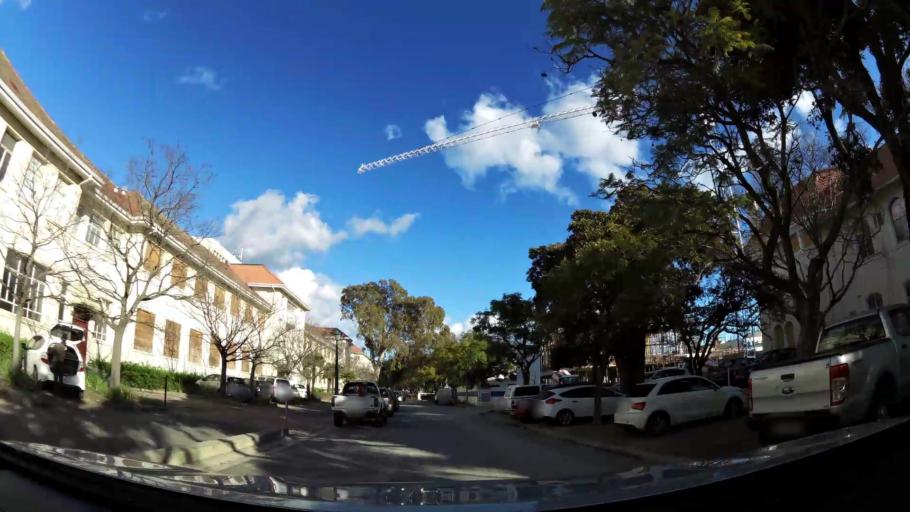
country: ZA
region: Western Cape
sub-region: Cape Winelands District Municipality
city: Stellenbosch
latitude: -33.9318
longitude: 18.8666
